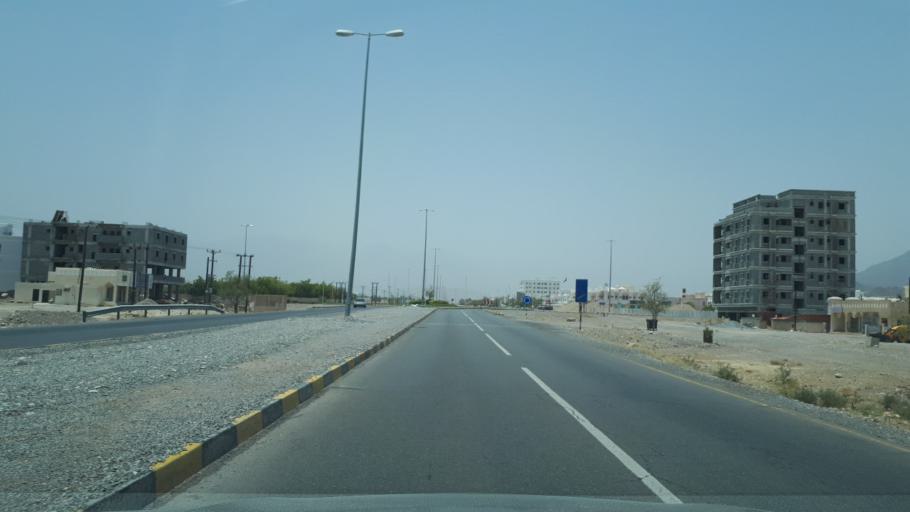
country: OM
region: Al Batinah
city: Rustaq
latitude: 23.4874
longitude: 57.4570
